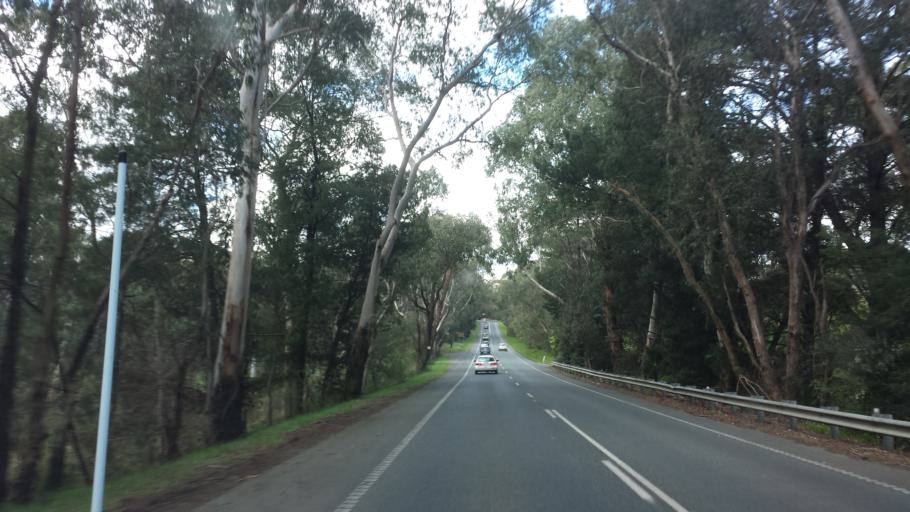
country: AU
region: Victoria
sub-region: Yarra Ranges
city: Selby
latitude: -37.9600
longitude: 145.3718
